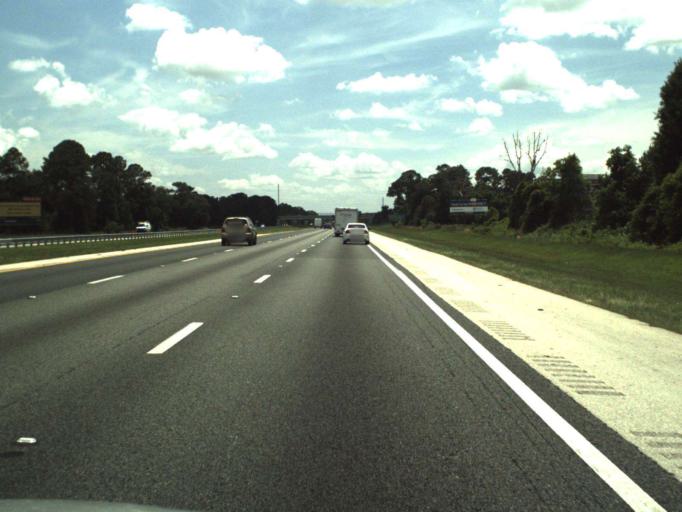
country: US
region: Florida
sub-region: Volusia County
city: Lake Helen
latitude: 28.9927
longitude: -81.2460
